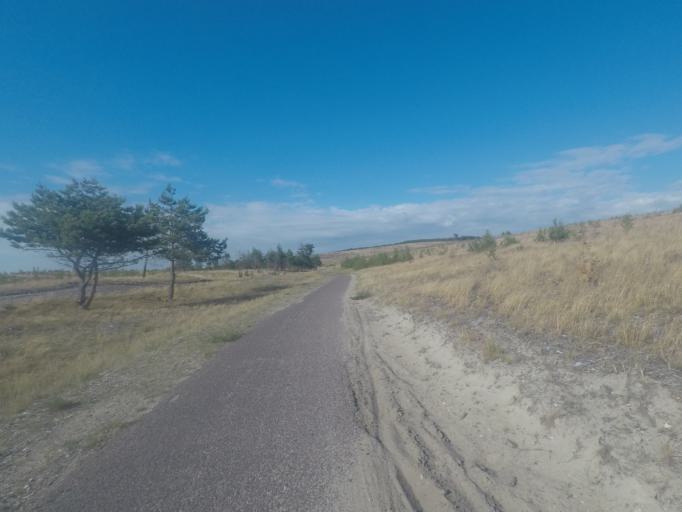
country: LT
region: Klaipedos apskritis
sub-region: Klaipeda
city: Klaipeda
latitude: 55.5913
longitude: 21.1133
